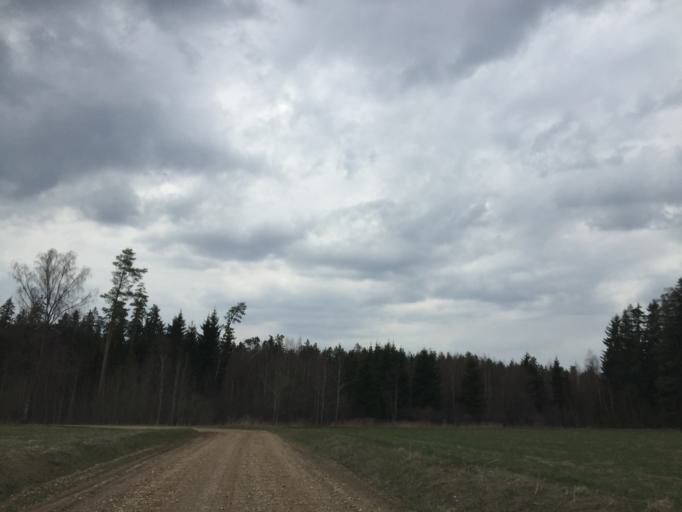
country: EE
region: Vorumaa
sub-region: Antsla vald
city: Vana-Antsla
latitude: 57.9413
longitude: 26.7249
